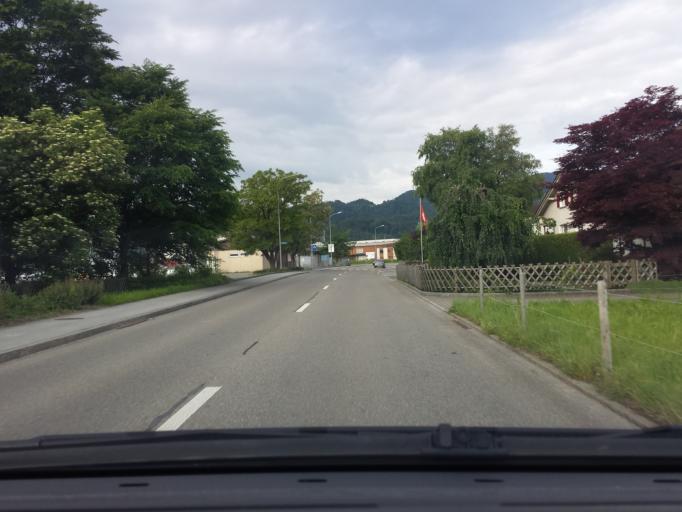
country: CH
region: Saint Gallen
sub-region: Wahlkreis Rheintal
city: Au
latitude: 47.4295
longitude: 9.6313
